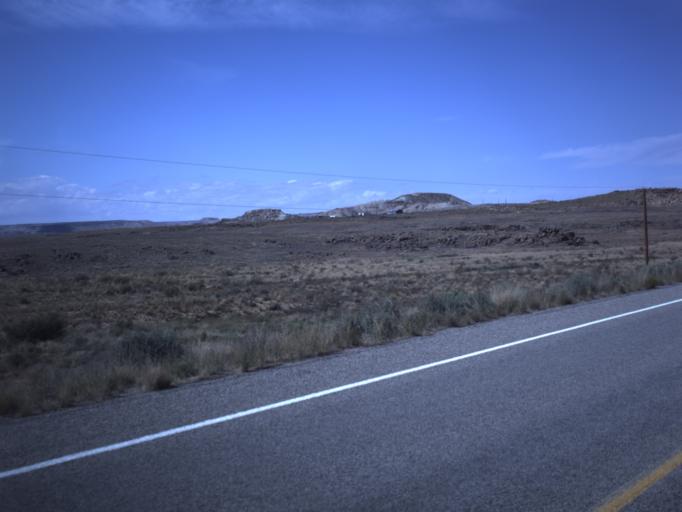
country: US
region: Colorado
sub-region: Montezuma County
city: Towaoc
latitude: 37.1615
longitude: -109.0688
